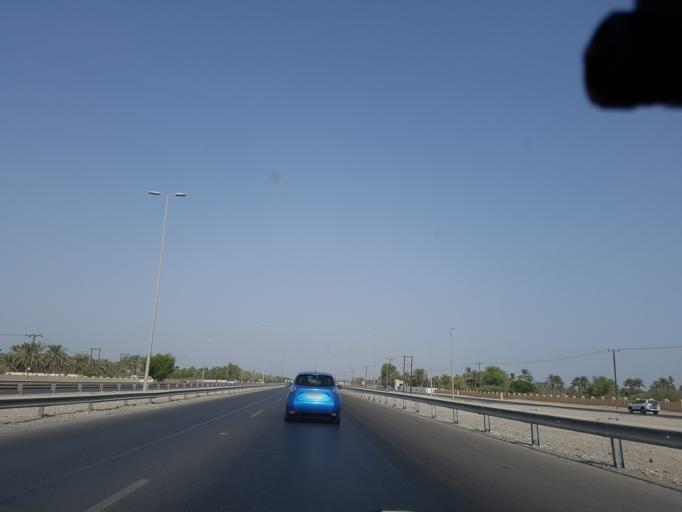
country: OM
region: Al Batinah
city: Barka'
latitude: 23.6718
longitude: 57.8645
